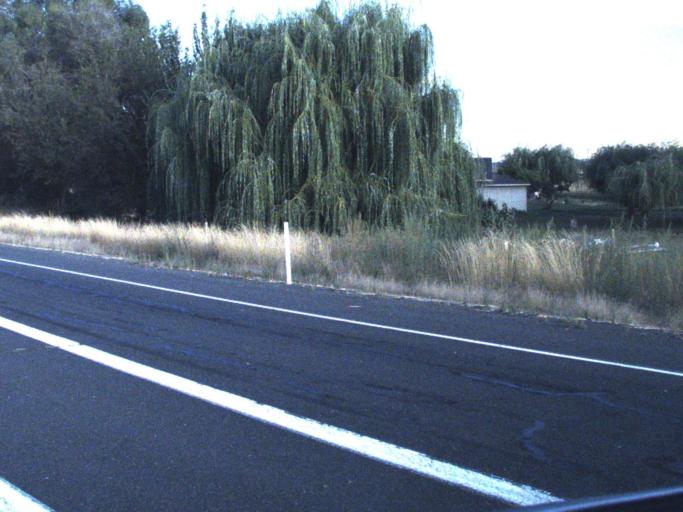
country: US
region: Washington
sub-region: Yakima County
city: Grandview
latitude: 46.2538
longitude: -119.8746
